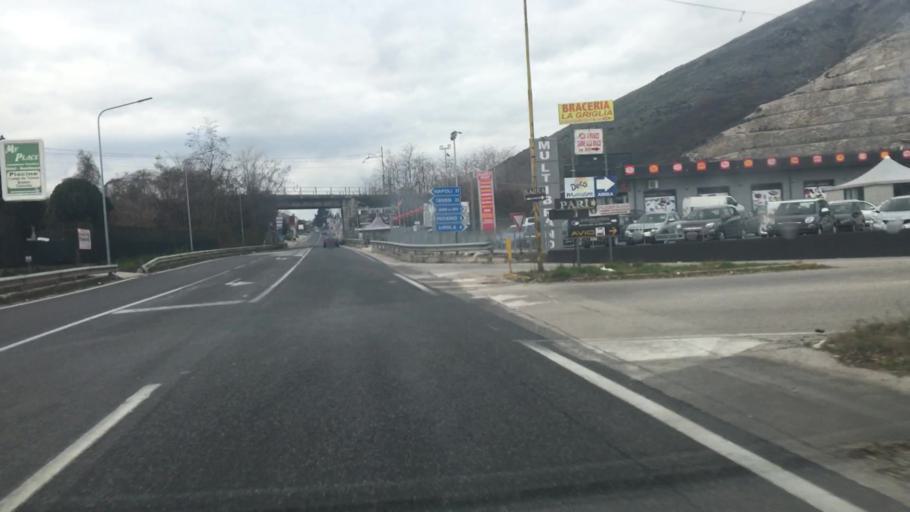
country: IT
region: Campania
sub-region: Provincia di Benevento
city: Arpaia
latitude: 41.0405
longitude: 14.5613
